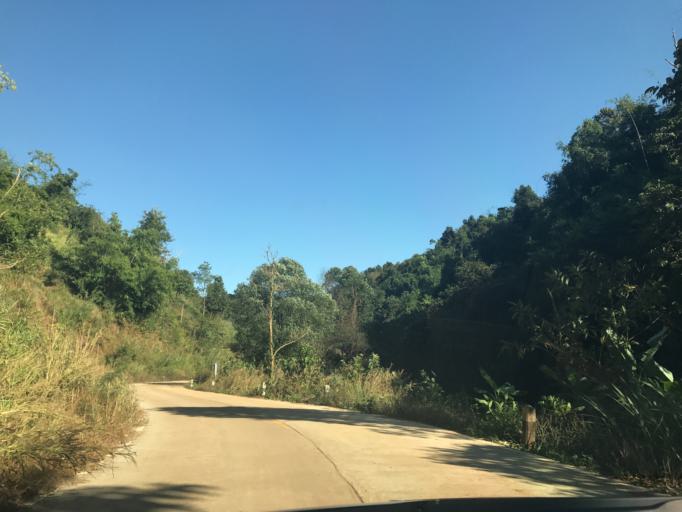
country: TH
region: Tak
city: Phop Phra
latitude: 16.5685
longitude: 98.8250
